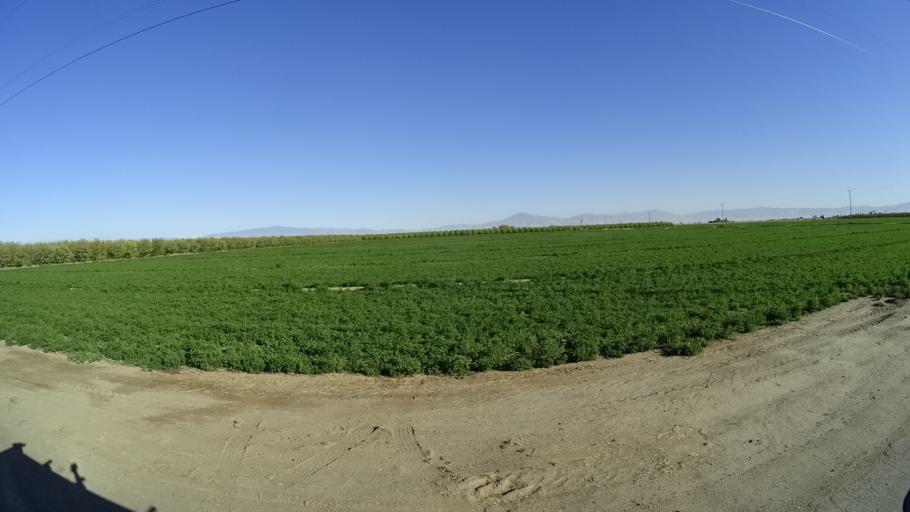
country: US
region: California
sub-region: Kern County
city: Greenacres
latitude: 35.2792
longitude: -119.1187
